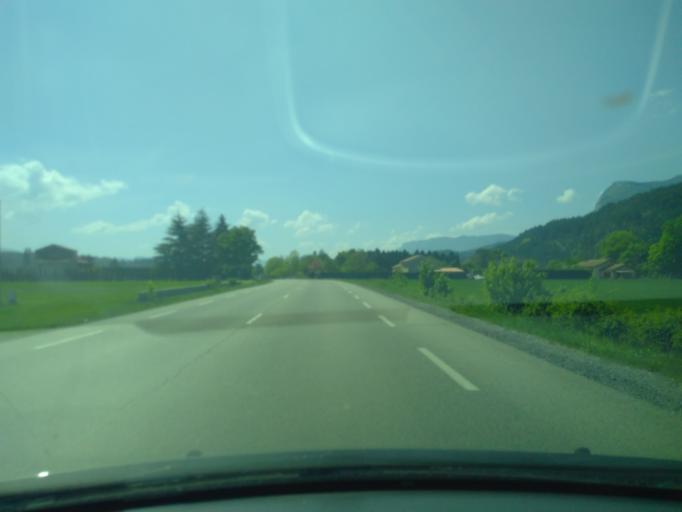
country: FR
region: Rhone-Alpes
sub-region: Departement de la Drome
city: Die
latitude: 44.7413
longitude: 5.3864
